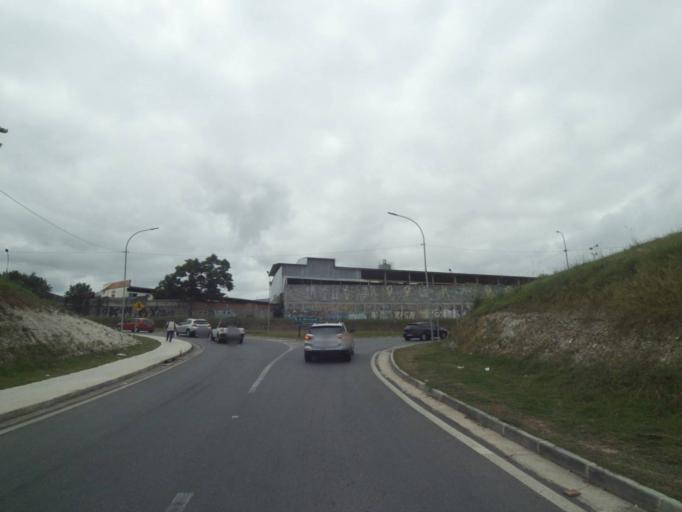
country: BR
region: Parana
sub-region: Pinhais
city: Pinhais
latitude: -25.3890
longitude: -49.1898
